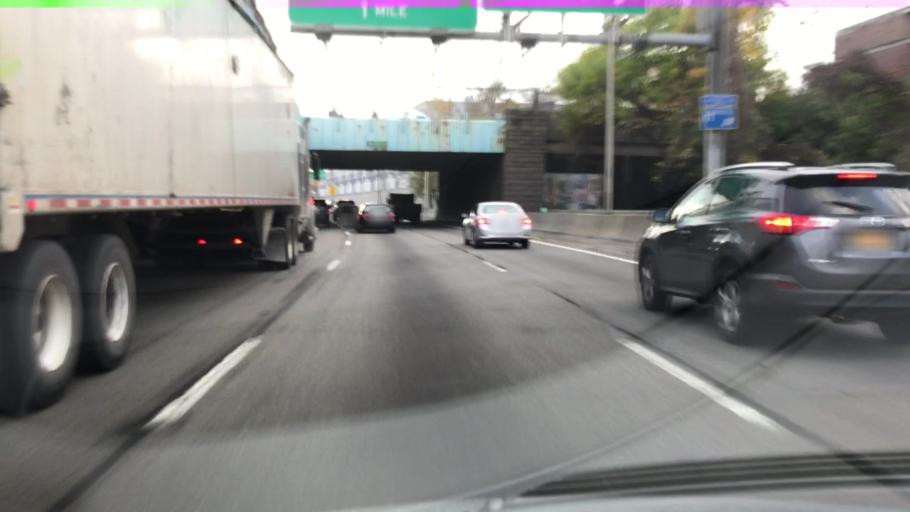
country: US
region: New York
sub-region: New York County
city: Inwood
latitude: 40.8789
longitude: -73.9034
